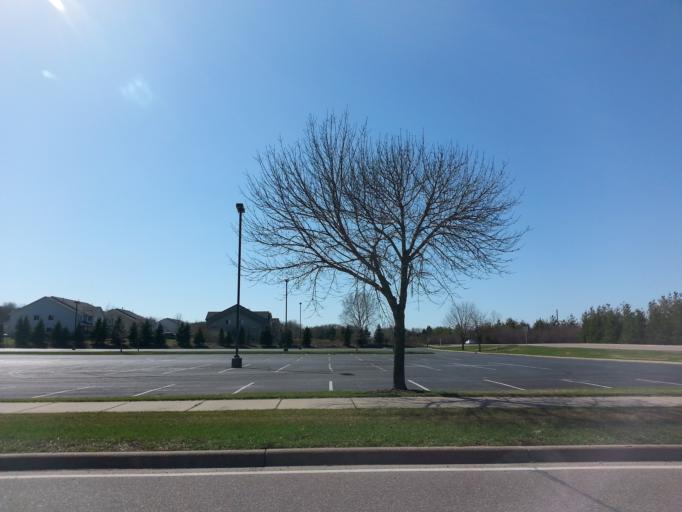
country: US
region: Minnesota
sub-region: Dakota County
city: Lakeville
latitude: 44.6520
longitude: -93.2992
